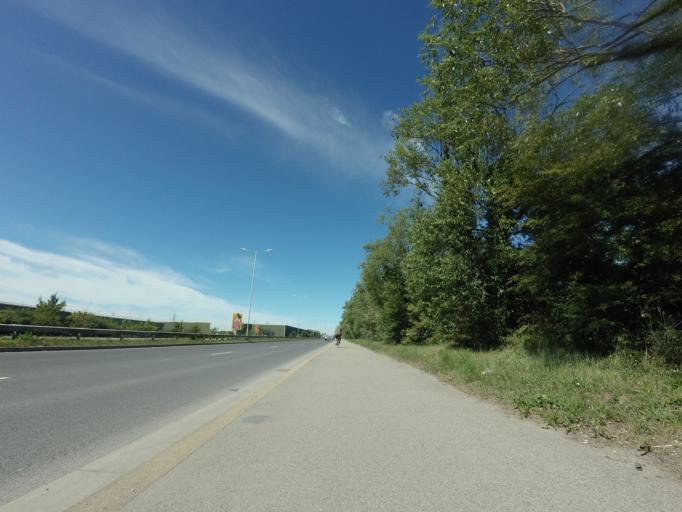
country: GB
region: England
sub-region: Kent
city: Sandwich
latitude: 51.3033
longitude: 1.3474
